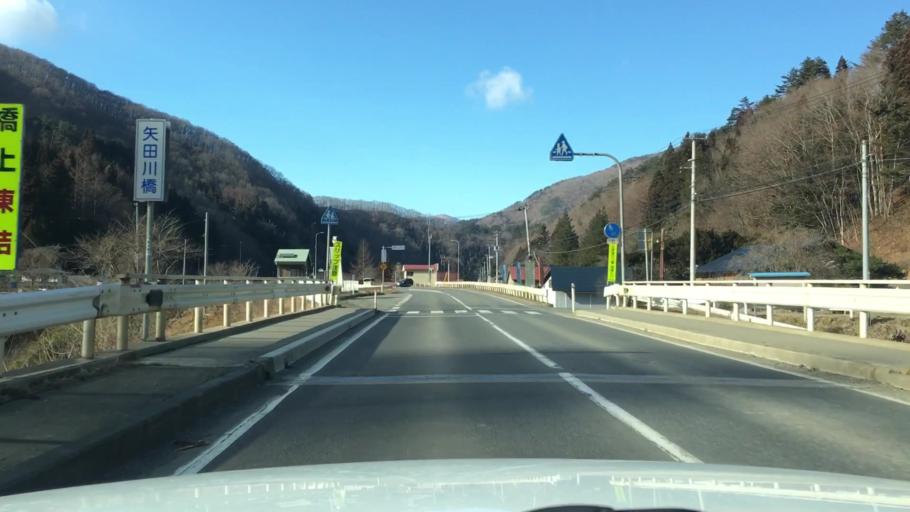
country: JP
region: Iwate
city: Tono
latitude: 39.6140
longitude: 141.6283
